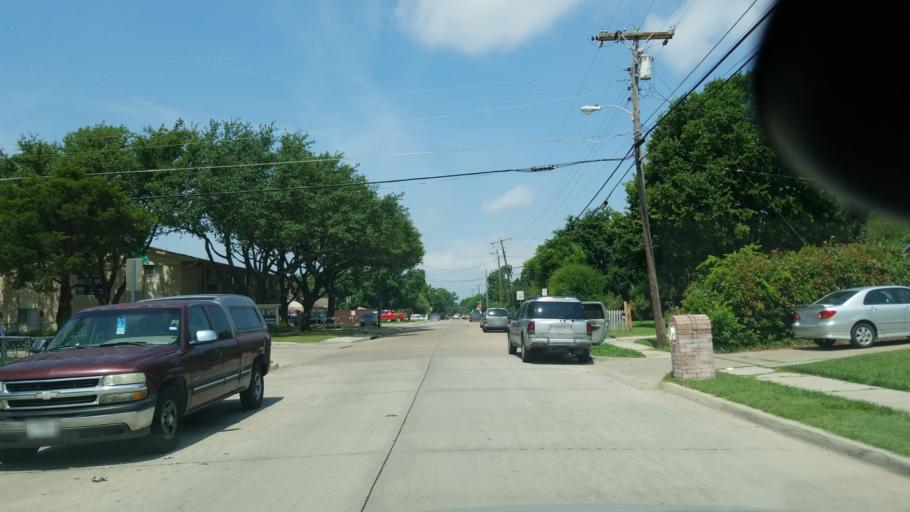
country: US
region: Texas
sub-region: Dallas County
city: Irving
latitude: 32.8276
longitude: -96.9437
